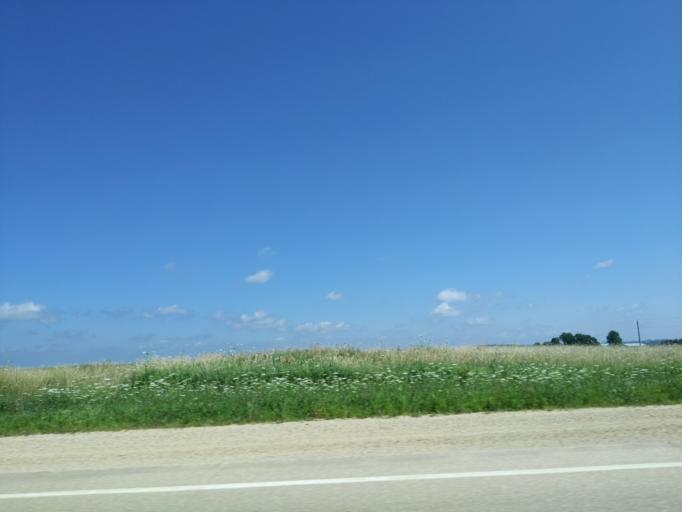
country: US
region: Wisconsin
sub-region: La Crosse County
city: La Crosse
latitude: 43.7319
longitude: -91.0949
